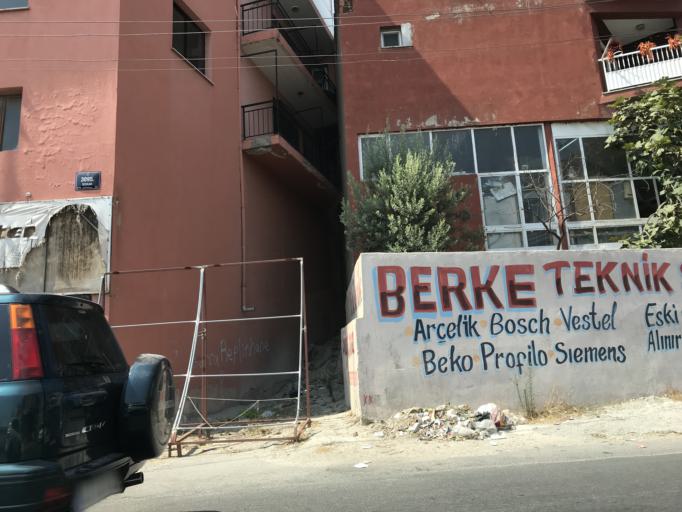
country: TR
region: Izmir
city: Karabaglar
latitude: 38.3836
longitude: 27.1241
